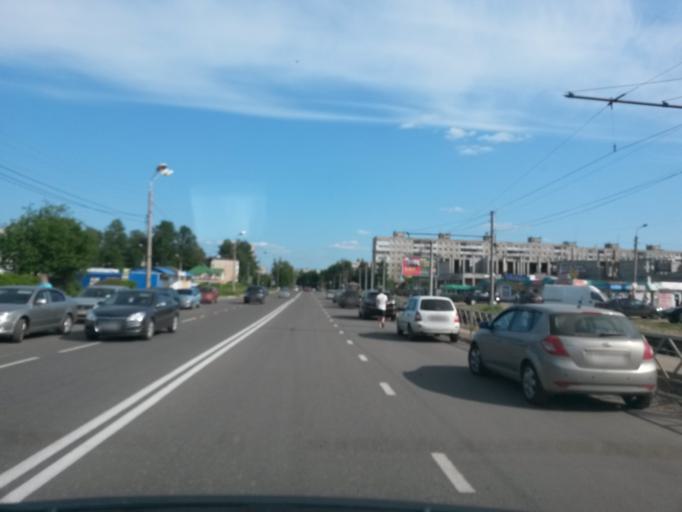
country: RU
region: Jaroslavl
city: Yaroslavl
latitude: 57.6859
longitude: 39.7665
